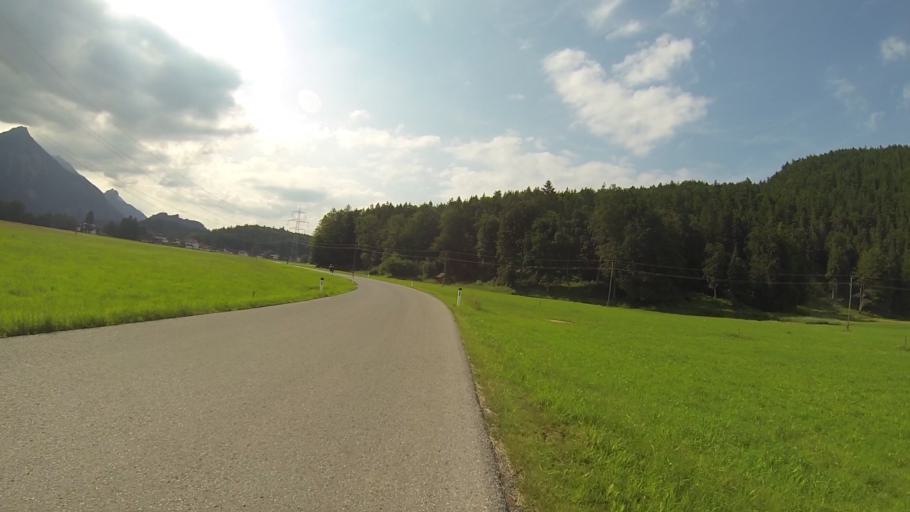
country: AT
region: Tyrol
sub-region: Politischer Bezirk Reutte
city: Pflach
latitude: 47.5339
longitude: 10.6960
